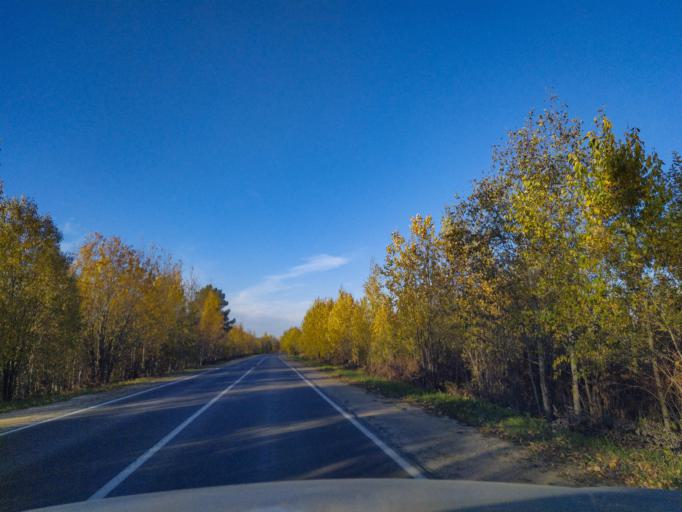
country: RU
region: Leningrad
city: Siverskiy
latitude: 59.3149
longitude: 30.0335
